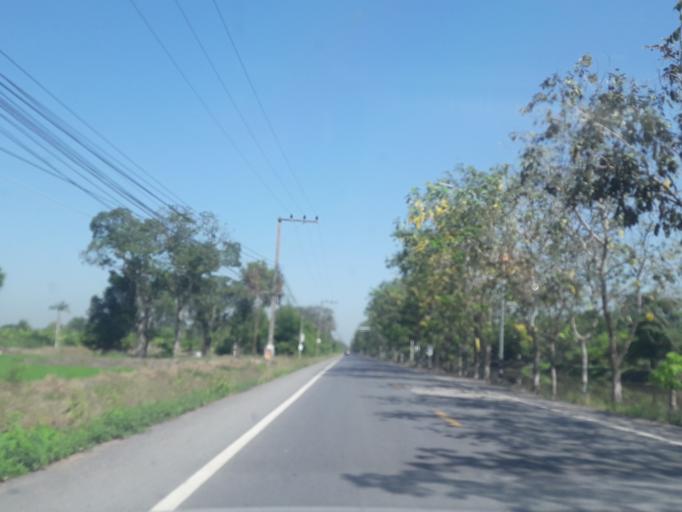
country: TH
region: Pathum Thani
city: Nong Suea
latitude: 14.1685
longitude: 100.8459
